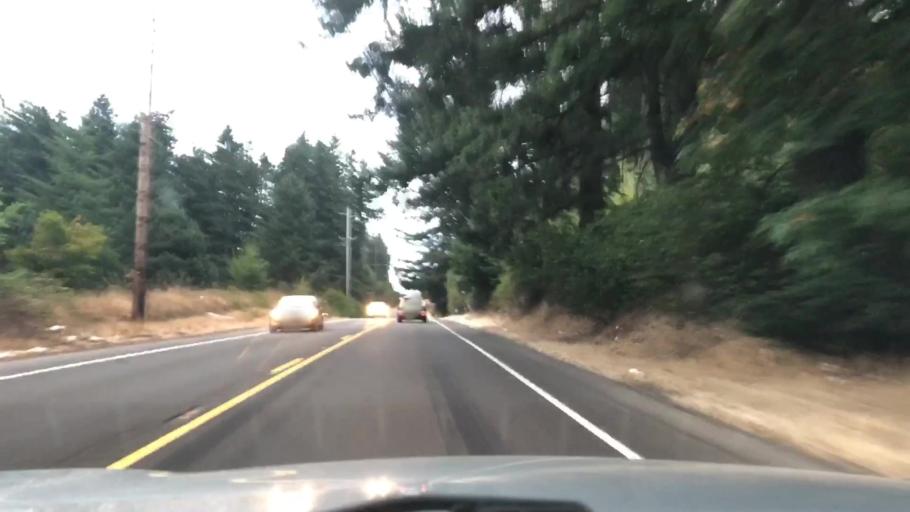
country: US
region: Oregon
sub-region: Clackamas County
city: Beavercreek
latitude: 45.2815
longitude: -122.5671
